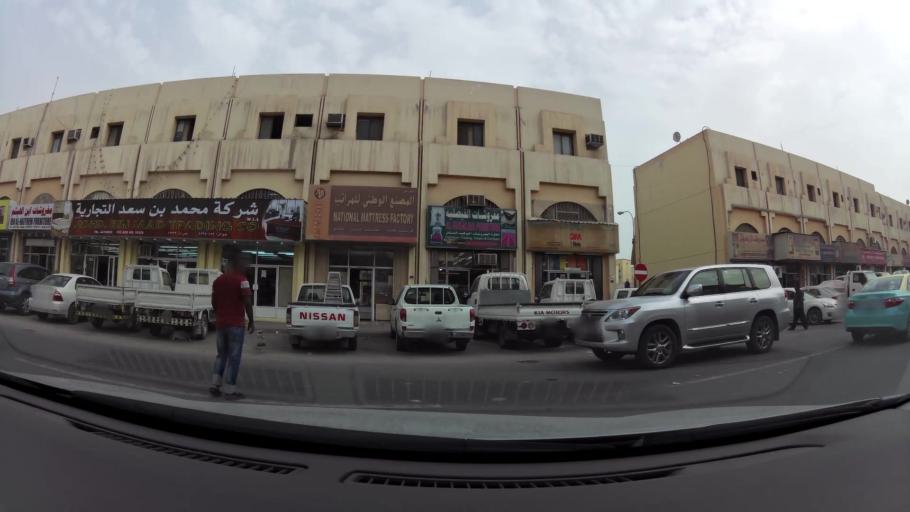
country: QA
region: Baladiyat ad Dawhah
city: Doha
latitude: 25.2696
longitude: 51.5399
